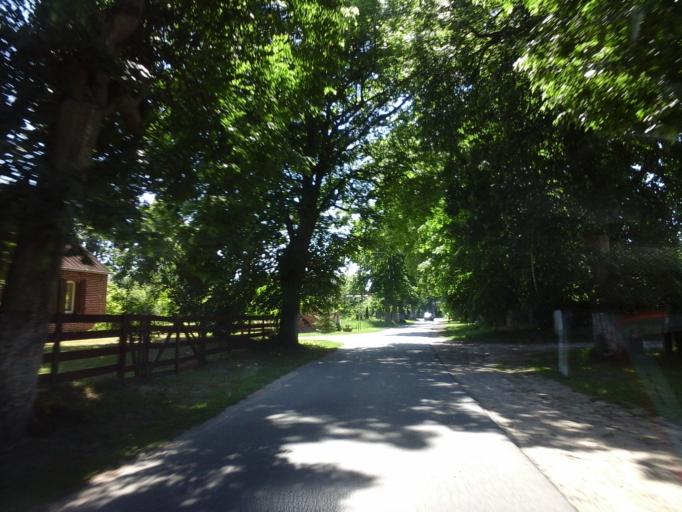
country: PL
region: West Pomeranian Voivodeship
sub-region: Powiat choszczenski
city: Drawno
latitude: 53.1342
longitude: 15.8500
